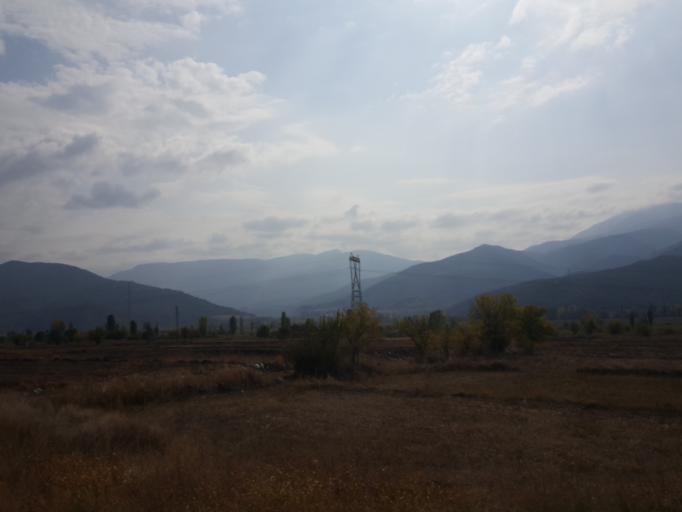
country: TR
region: Corum
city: Hacihamza
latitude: 41.1181
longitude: 34.4051
